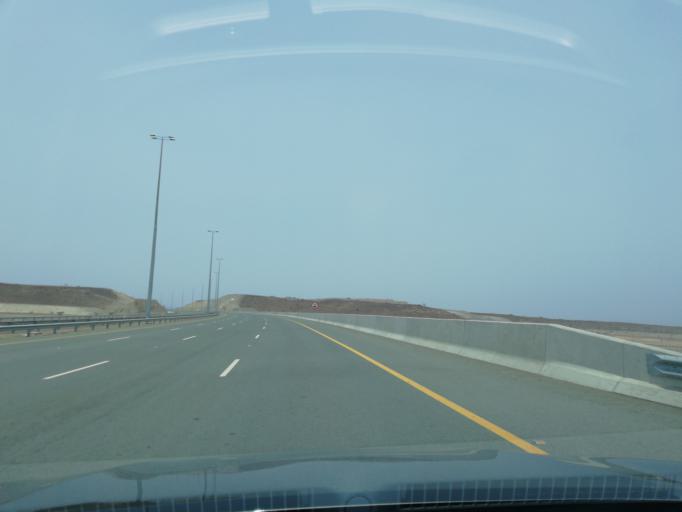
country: OM
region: Al Batinah
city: Al Liwa'
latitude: 24.5381
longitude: 56.4985
